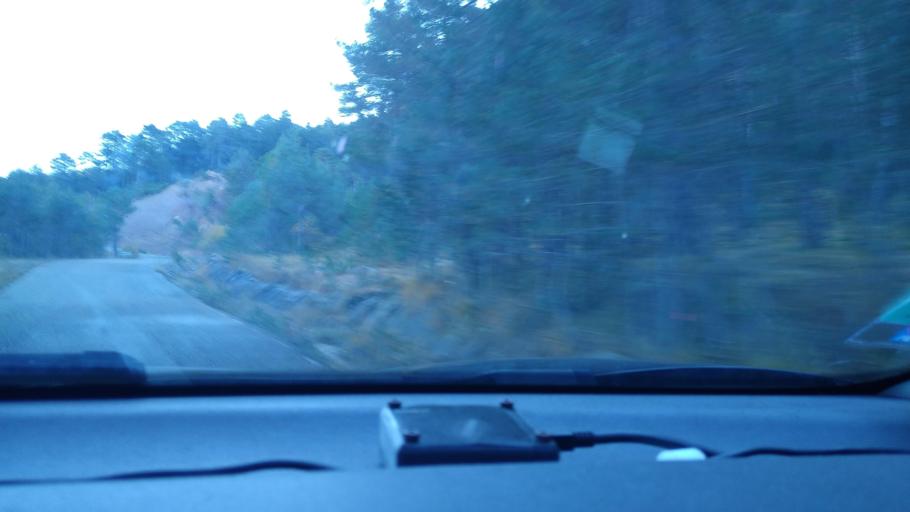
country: ES
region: Catalonia
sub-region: Provincia de Barcelona
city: Saldes
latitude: 42.2044
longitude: 1.7299
